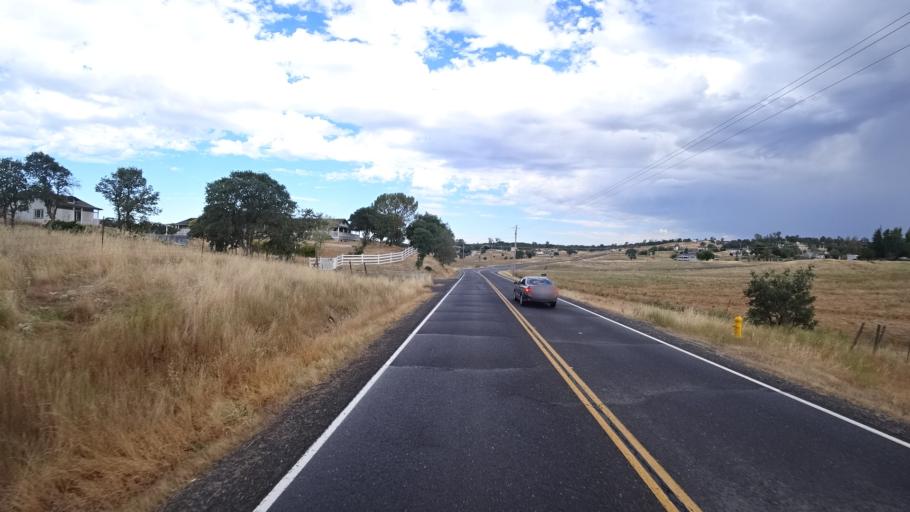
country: US
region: California
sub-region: Calaveras County
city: Copperopolis
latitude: 37.9306
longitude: -120.6420
